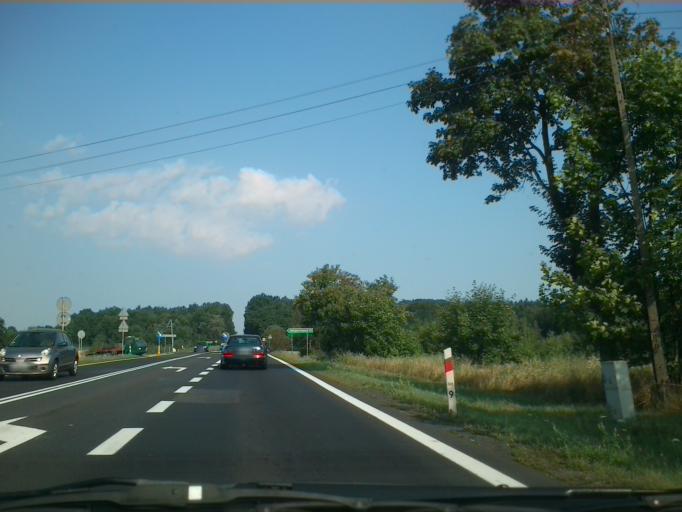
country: PL
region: Lower Silesian Voivodeship
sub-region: Powiat polkowicki
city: Gaworzyce
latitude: 51.6606
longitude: 15.8247
